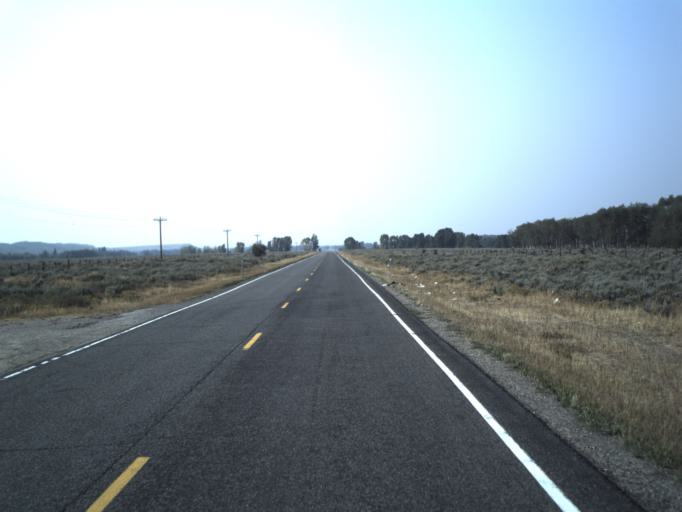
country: US
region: Wyoming
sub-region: Uinta County
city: Evanston
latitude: 40.9682
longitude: -110.8480
